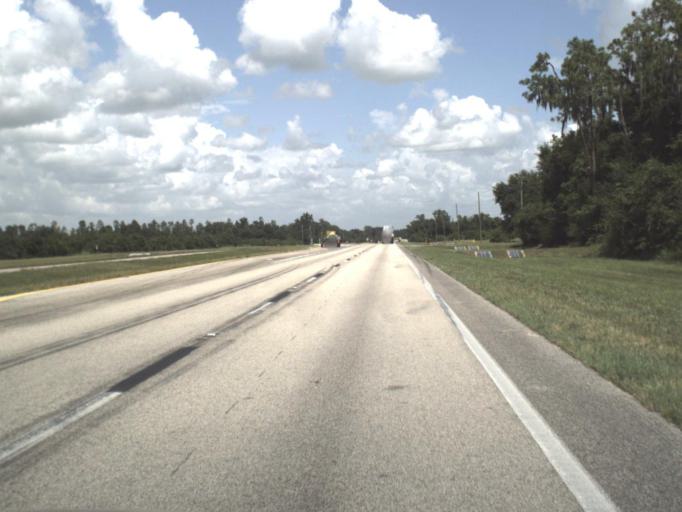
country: US
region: Florida
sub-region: Hardee County
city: Bowling Green
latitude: 27.6520
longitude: -81.8227
